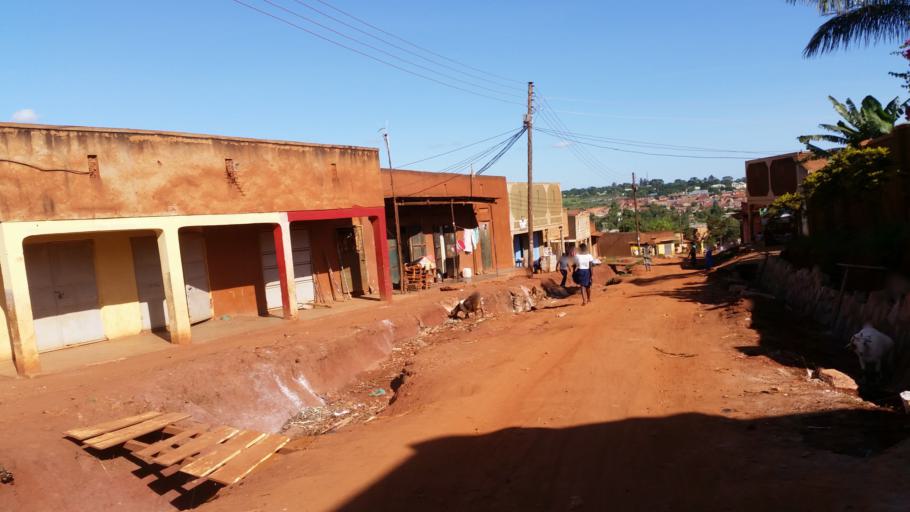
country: UG
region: Central Region
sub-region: Wakiso District
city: Kireka
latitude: 0.3332
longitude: 32.6525
